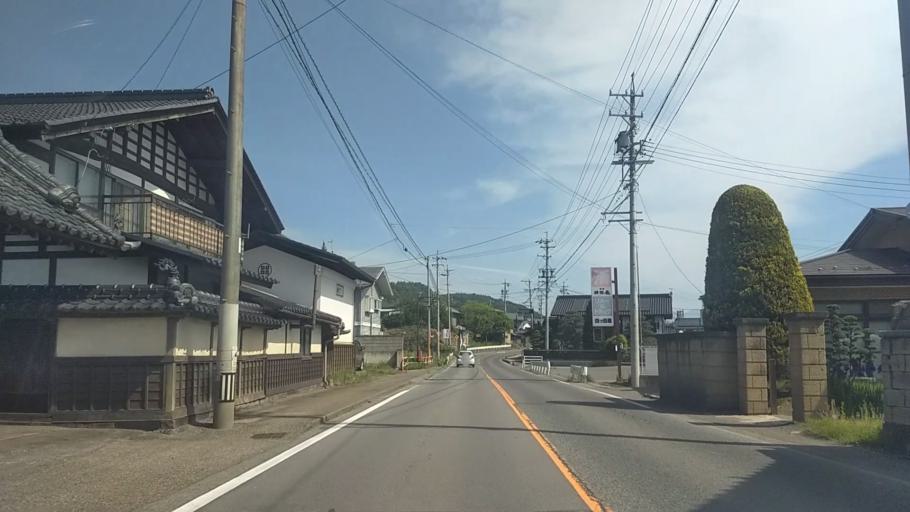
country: JP
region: Nagano
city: Saku
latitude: 36.1343
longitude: 138.4713
